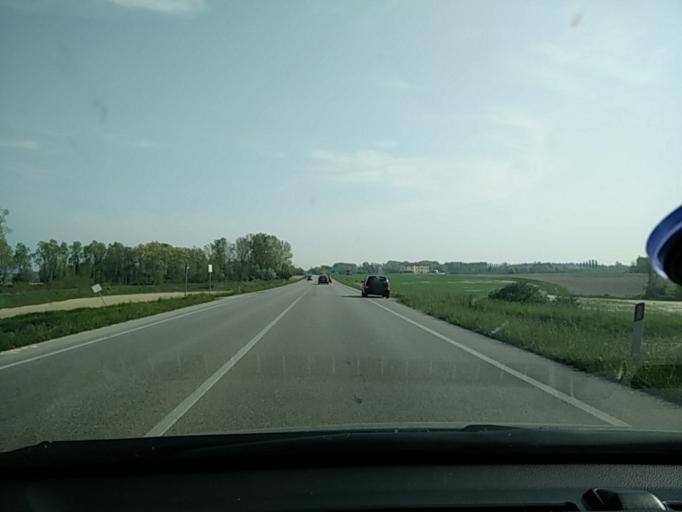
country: IT
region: Friuli Venezia Giulia
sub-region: Provincia di Pordenone
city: Prata di Sotto
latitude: 45.9042
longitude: 12.6162
